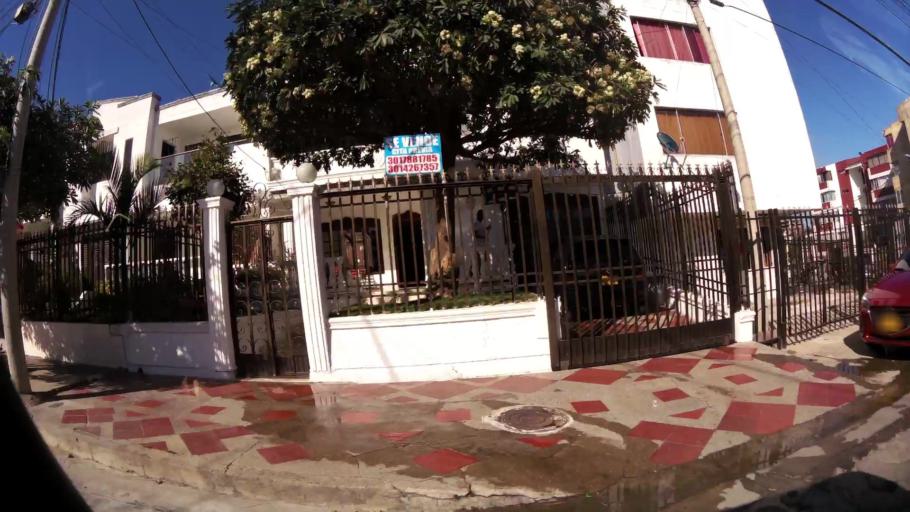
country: CO
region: Atlantico
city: Barranquilla
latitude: 10.9948
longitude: -74.8296
